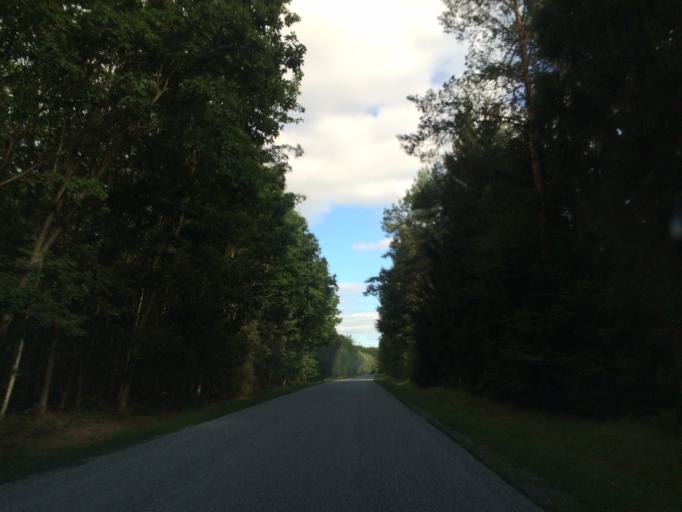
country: FR
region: Alsace
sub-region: Departement du Bas-Rhin
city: Soufflenheim
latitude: 48.8536
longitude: 7.9394
